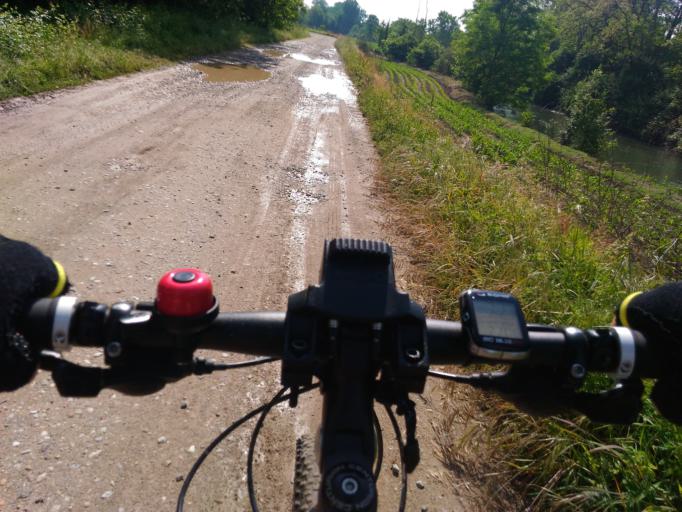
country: IT
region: Lombardy
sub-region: Provincia di Lodi
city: San Martino in Strada
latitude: 45.2674
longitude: 9.5204
